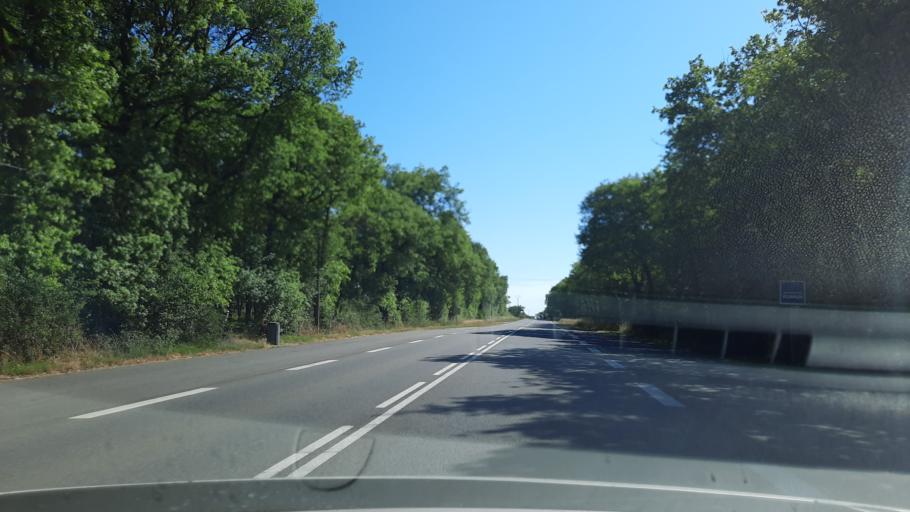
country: FR
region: Midi-Pyrenees
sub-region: Departement du Tarn-et-Garonne
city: Caylus
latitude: 44.2052
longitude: 1.7132
